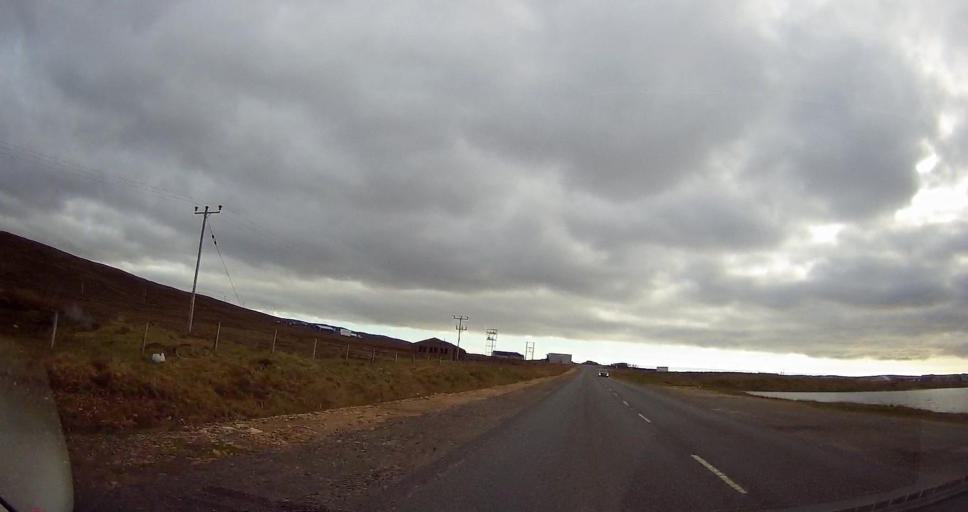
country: GB
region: Scotland
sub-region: Shetland Islands
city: Lerwick
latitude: 60.4423
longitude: -1.2624
